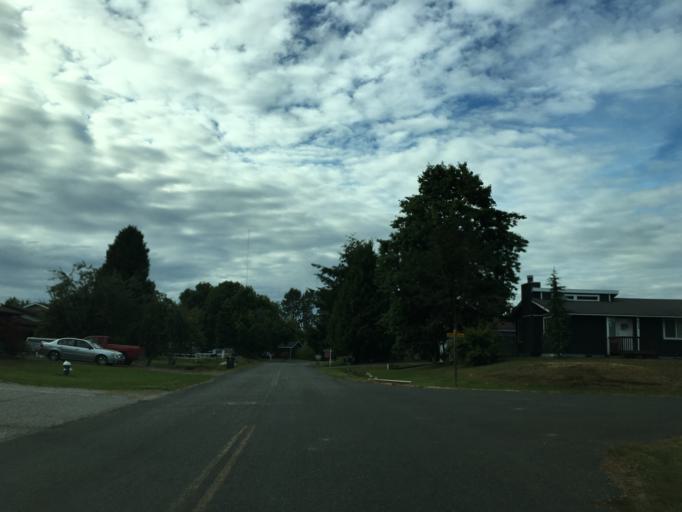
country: US
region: Washington
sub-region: Whatcom County
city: Birch Bay
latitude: 48.9481
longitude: -122.7420
